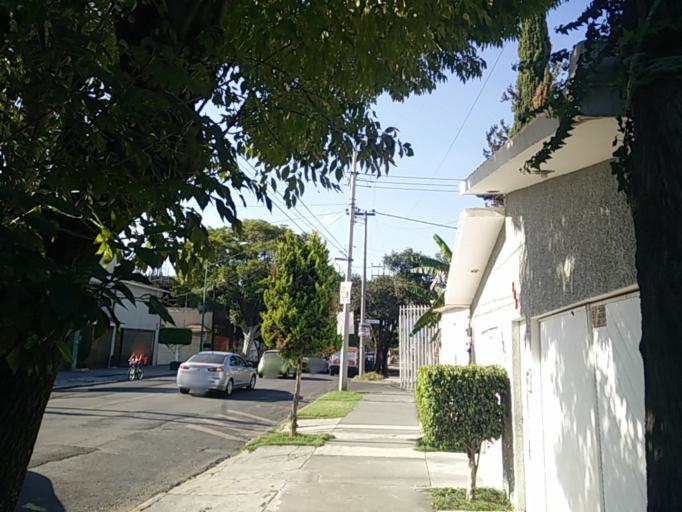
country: MX
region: Mexico
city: Colonia Lindavista
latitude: 19.4976
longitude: -99.1308
